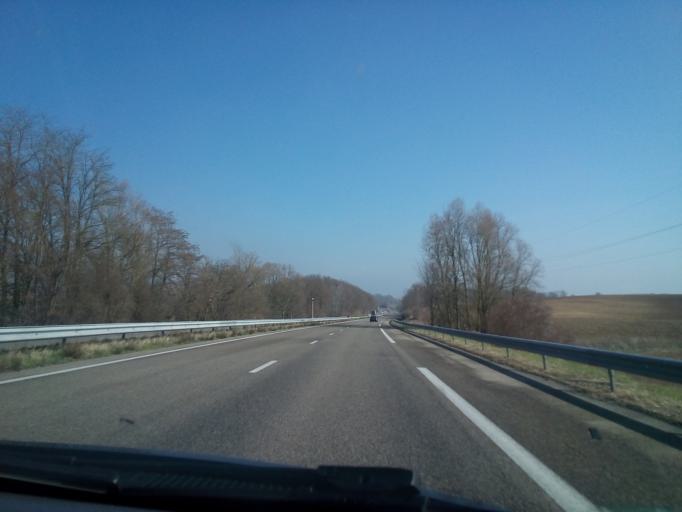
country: DE
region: Rheinland-Pfalz
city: Scheibenhardt
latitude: 48.9408
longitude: 8.1301
